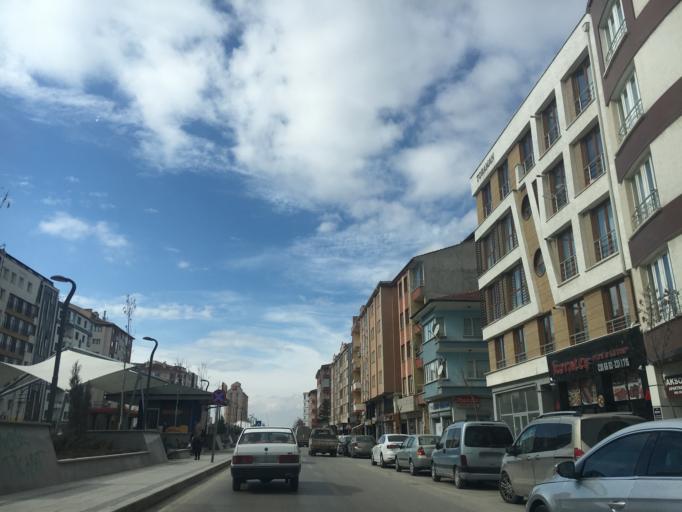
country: TR
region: Eskisehir
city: Eskisehir
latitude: 39.7818
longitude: 30.5177
